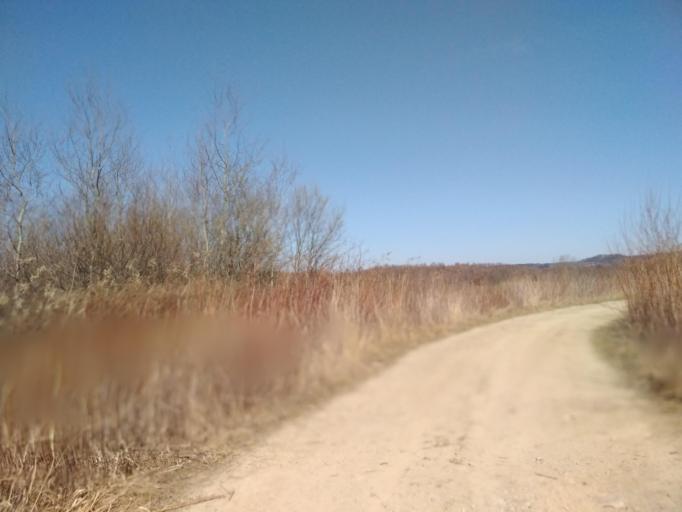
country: PL
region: Subcarpathian Voivodeship
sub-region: Powiat brzozowski
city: Orzechowka
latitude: 49.7226
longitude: 21.9688
